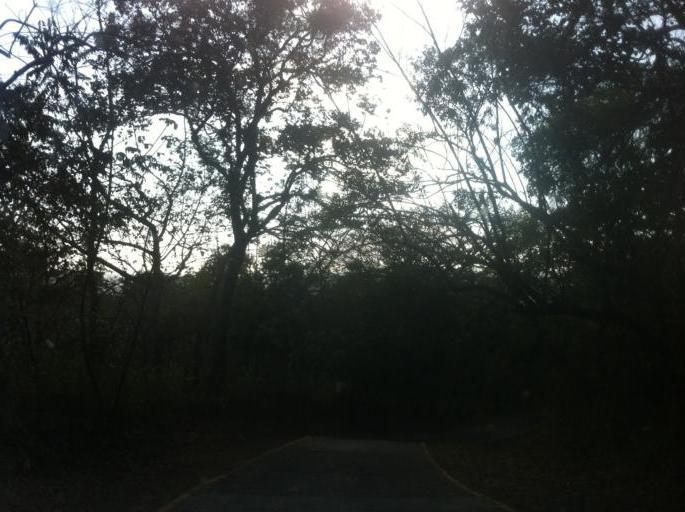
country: NI
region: Granada
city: Diriomo
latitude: 11.8413
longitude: -86.0004
